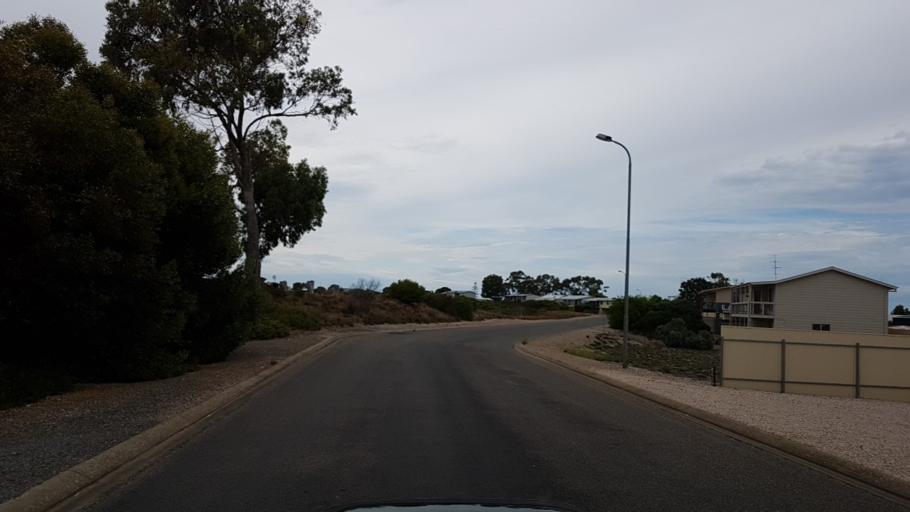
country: AU
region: South Australia
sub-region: Yorke Peninsula
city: Port Victoria
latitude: -34.9084
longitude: 137.0522
